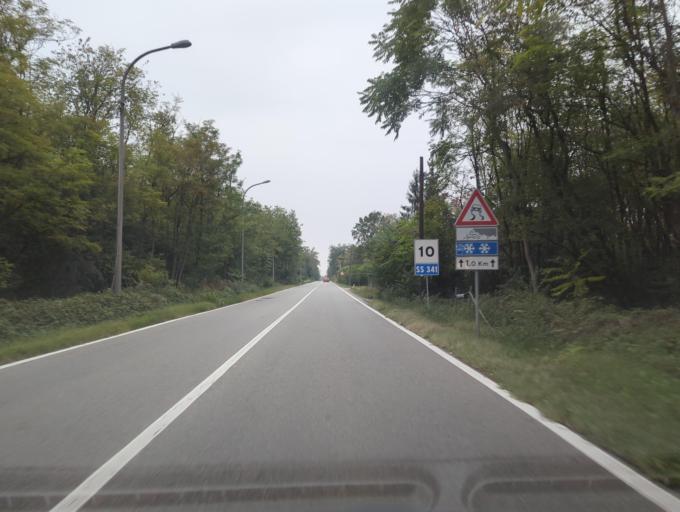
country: IT
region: Piedmont
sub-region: Provincia di Novara
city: Galliate
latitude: 45.4992
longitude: 8.7195
